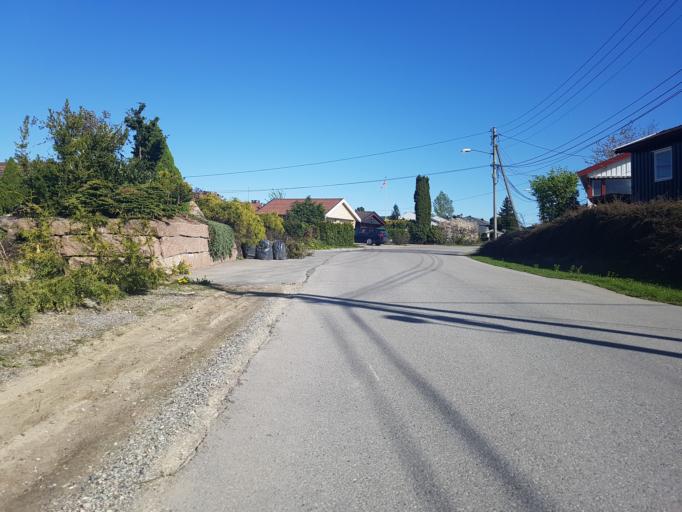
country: NO
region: Buskerud
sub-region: Drammen
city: Drammen
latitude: 59.7226
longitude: 10.2106
